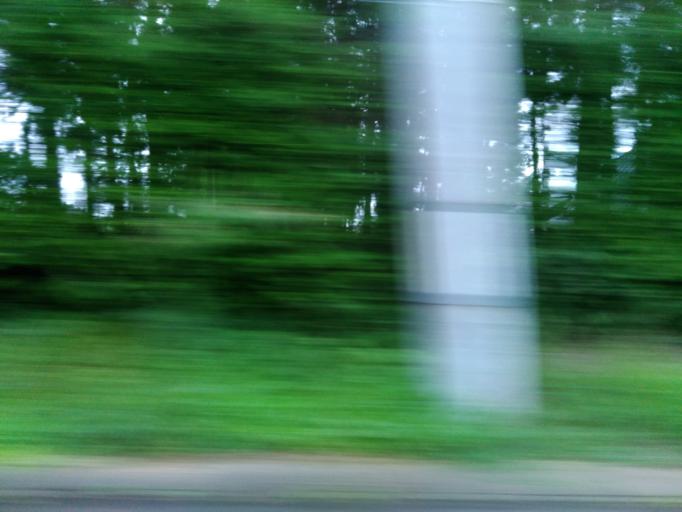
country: JP
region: Fukushima
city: Namie
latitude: 37.6320
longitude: 140.9280
